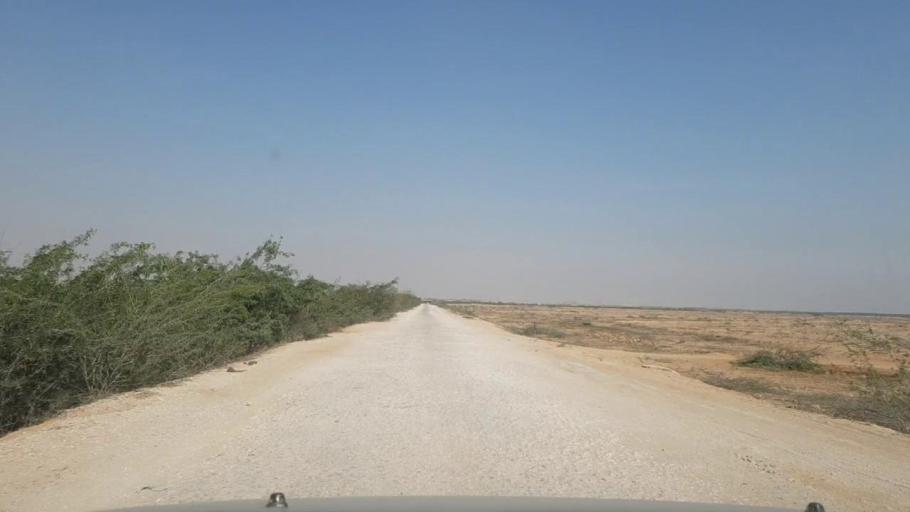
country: PK
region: Sindh
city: Thatta
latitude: 24.9680
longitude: 67.9652
